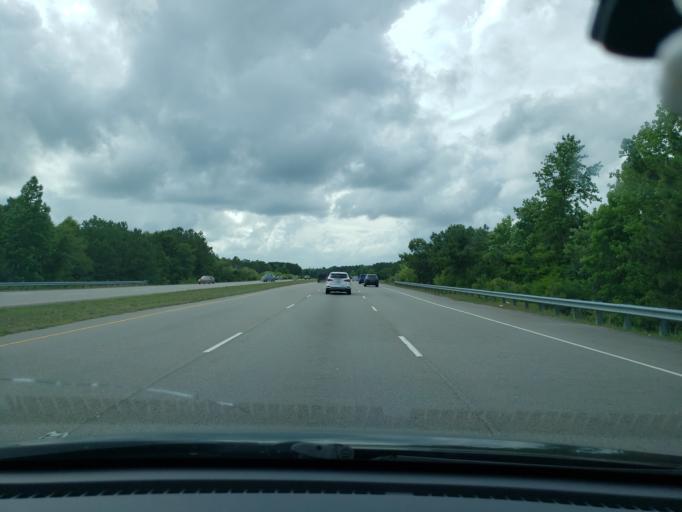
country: US
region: North Carolina
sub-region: New Hanover County
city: Kings Grant
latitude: 34.2542
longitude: -77.9003
